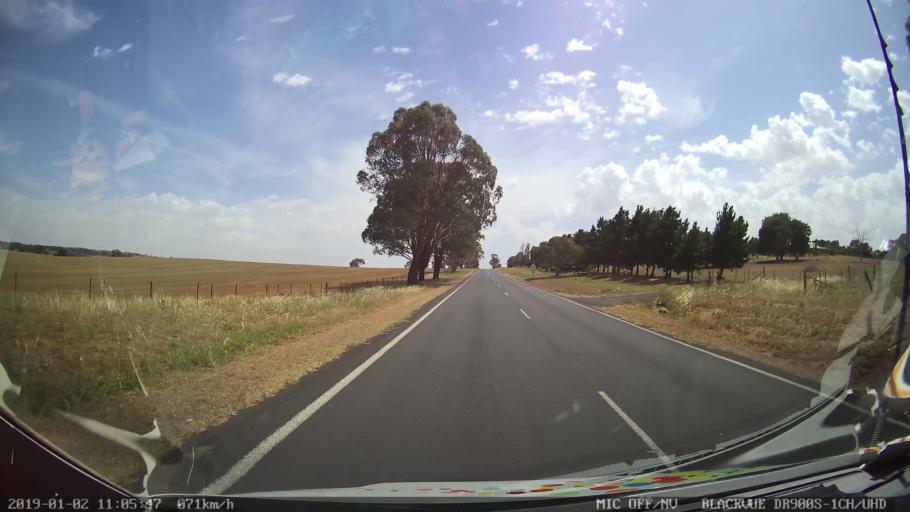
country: AU
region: New South Wales
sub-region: Young
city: Young
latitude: -34.5610
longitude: 148.3540
